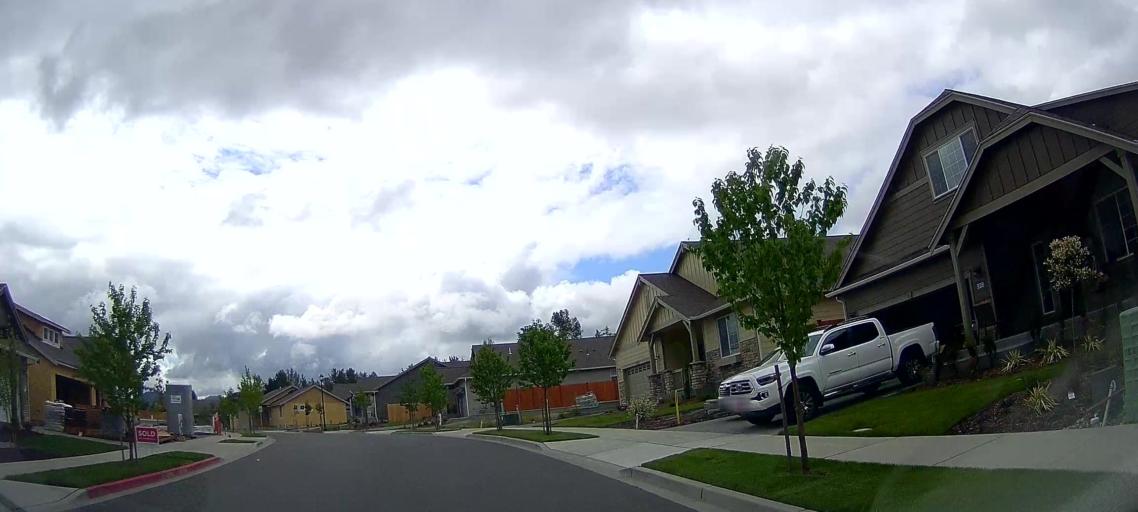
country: US
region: Washington
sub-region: Skagit County
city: Big Lake
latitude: 48.4152
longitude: -122.2803
